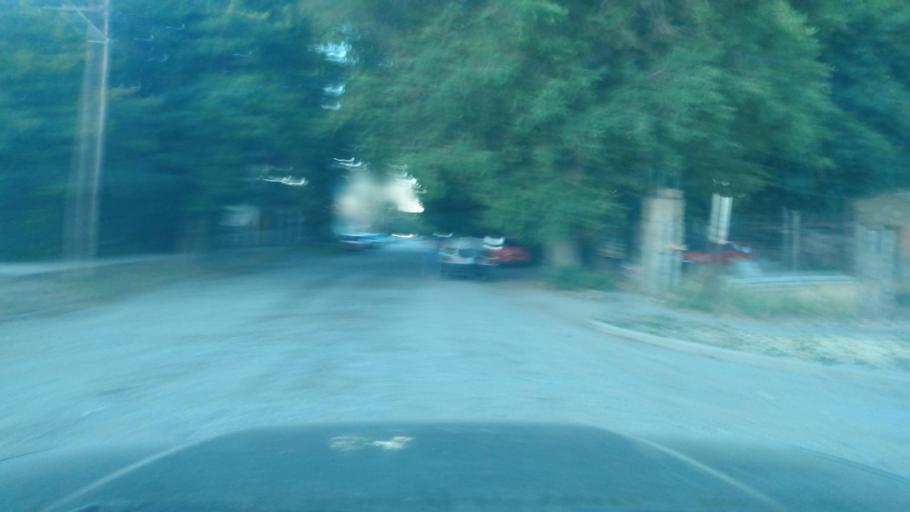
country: AR
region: Neuquen
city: Junin de los Andes
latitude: -39.9541
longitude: -71.0742
